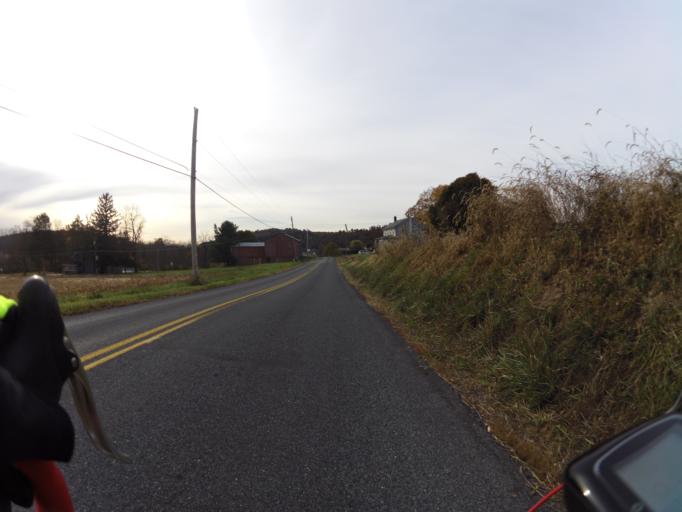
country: US
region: Pennsylvania
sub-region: Union County
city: New Columbia
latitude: 41.0413
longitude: -76.9480
